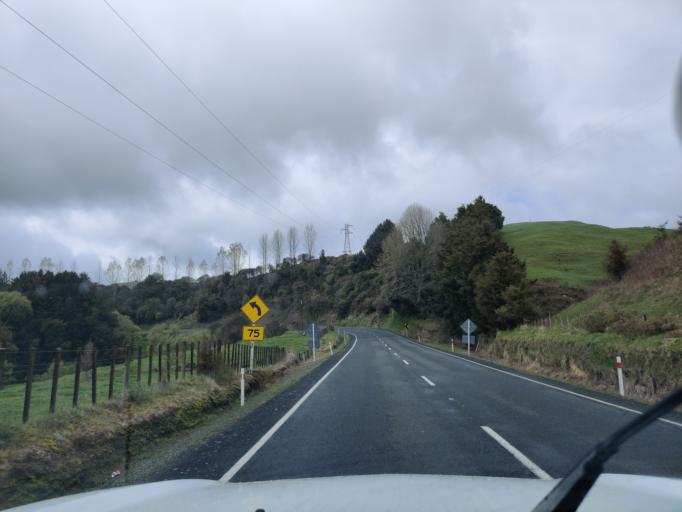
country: NZ
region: Waikato
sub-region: Otorohanga District
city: Otorohanga
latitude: -38.6956
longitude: 175.2202
